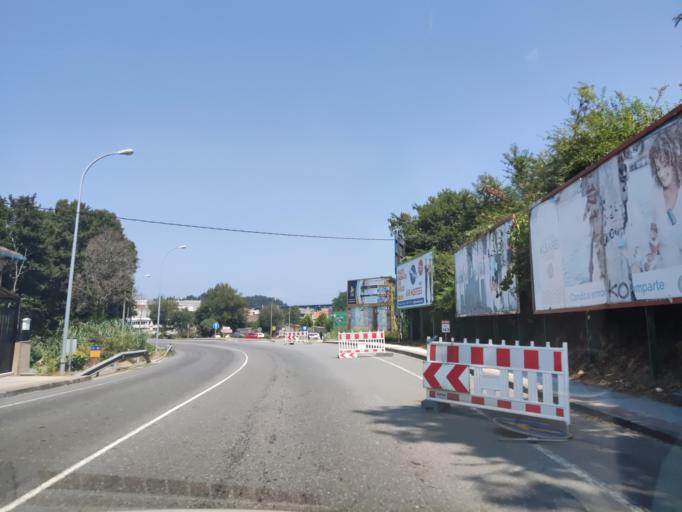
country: ES
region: Galicia
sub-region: Provincia de Pontevedra
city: Redondela
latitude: 42.2763
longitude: -8.6102
